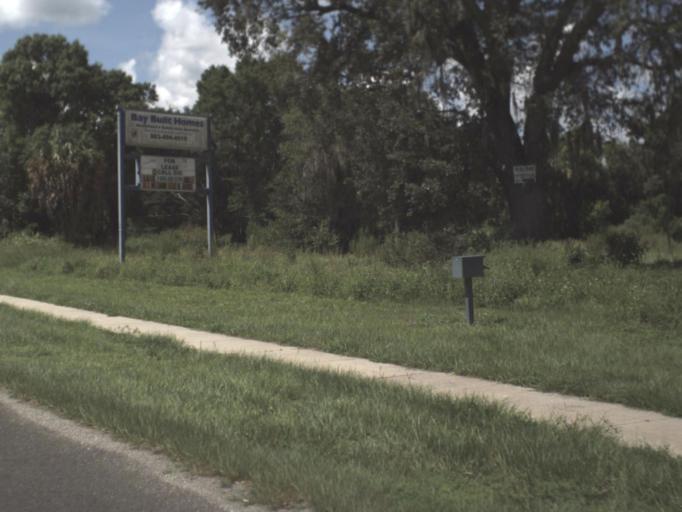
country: US
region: Florida
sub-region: DeSoto County
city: Arcadia
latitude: 27.2021
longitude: -81.8632
